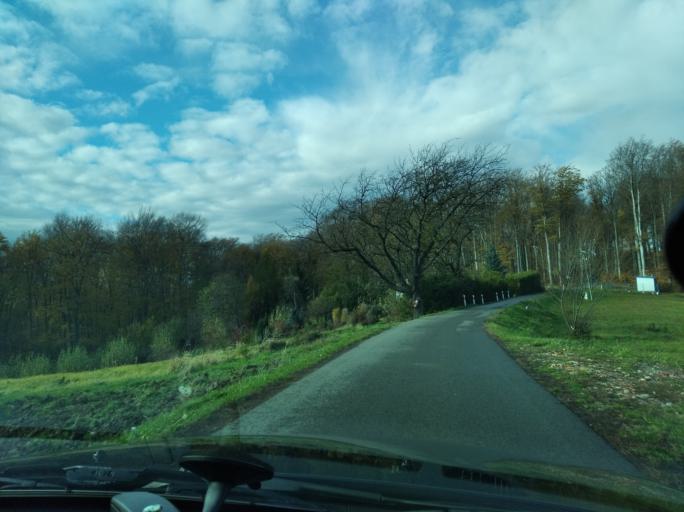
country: PL
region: Subcarpathian Voivodeship
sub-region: Powiat debicki
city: Debica
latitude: 50.0303
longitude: 21.4578
